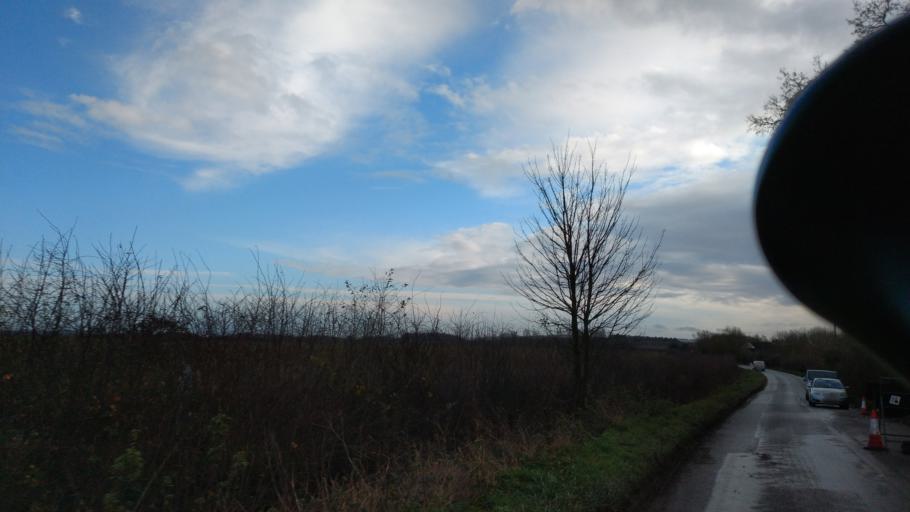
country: GB
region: England
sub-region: Borough of Swindon
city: Highworth
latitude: 51.6235
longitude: -1.7063
